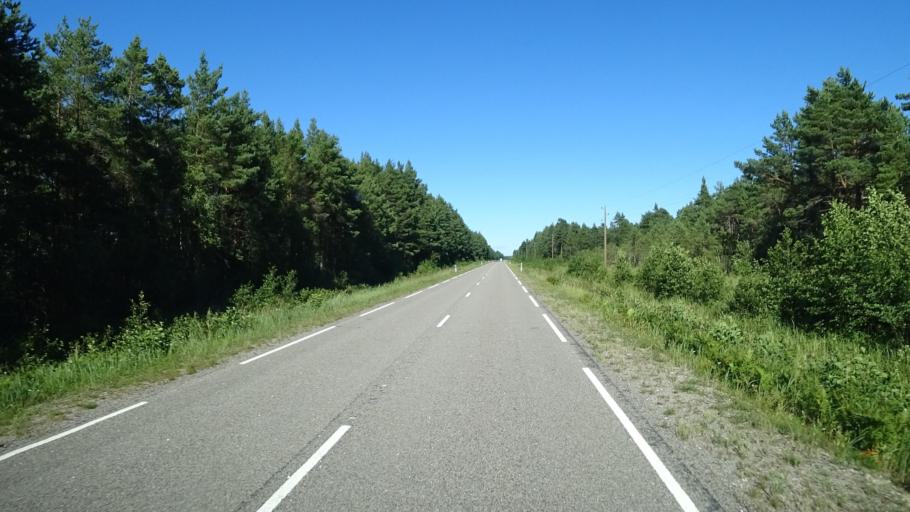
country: LV
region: Dundaga
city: Dundaga
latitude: 57.7033
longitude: 22.4271
